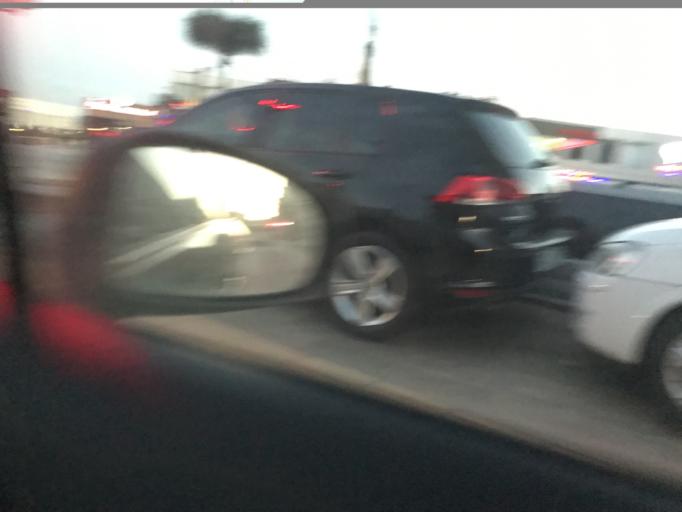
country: TR
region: Istanbul
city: Pendik
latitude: 40.9082
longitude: 29.2932
